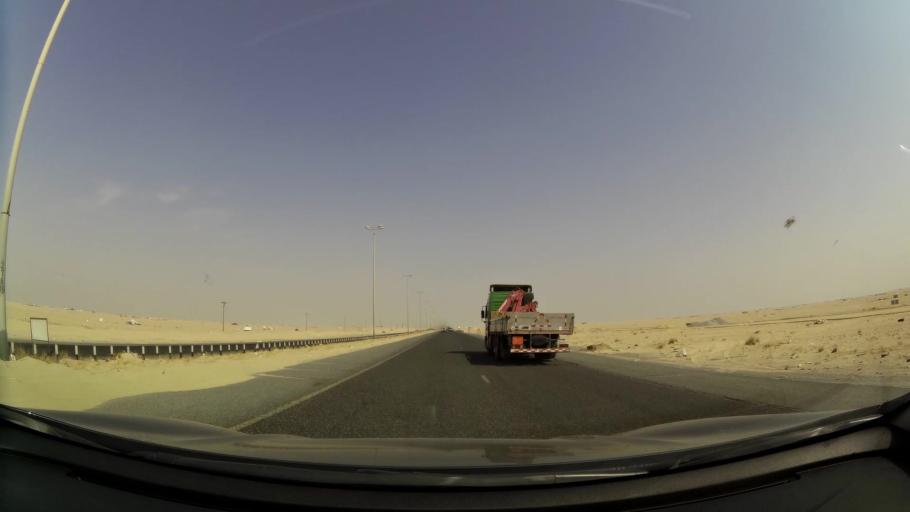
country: KW
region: Al Ahmadi
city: Al Wafrah
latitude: 28.8217
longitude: 48.0488
